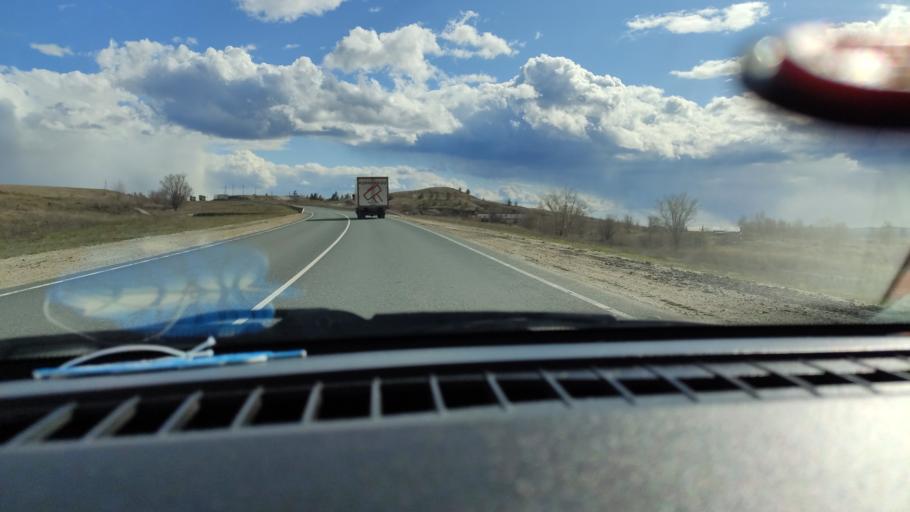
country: RU
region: Saratov
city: Alekseyevka
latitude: 52.3242
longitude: 47.9206
